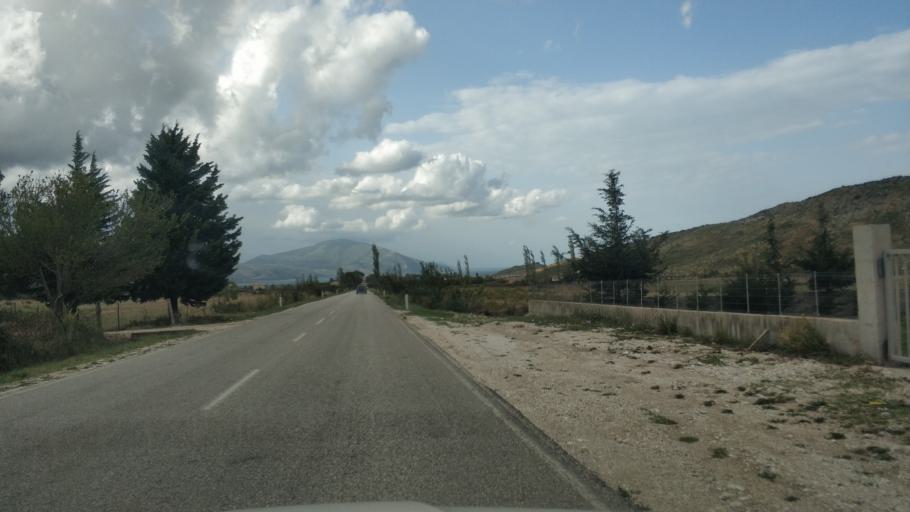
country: AL
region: Vlore
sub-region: Rrethi i Vlores
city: Orikum
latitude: 40.2737
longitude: 19.5101
